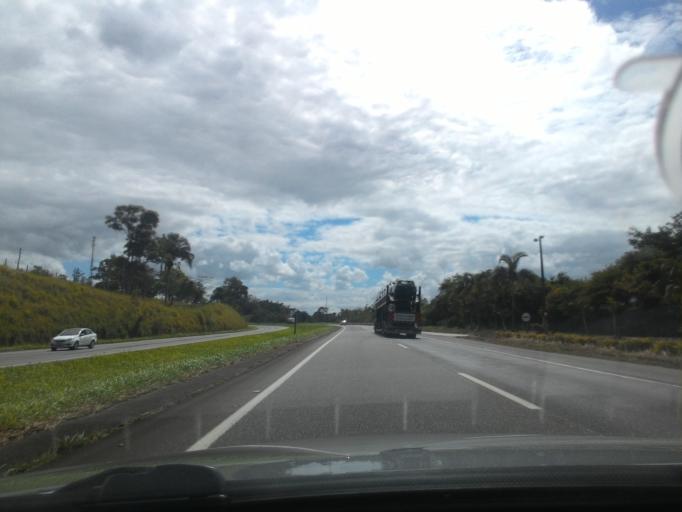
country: BR
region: Sao Paulo
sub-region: Jacupiranga
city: Jacupiranga
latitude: -24.6539
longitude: -47.9598
